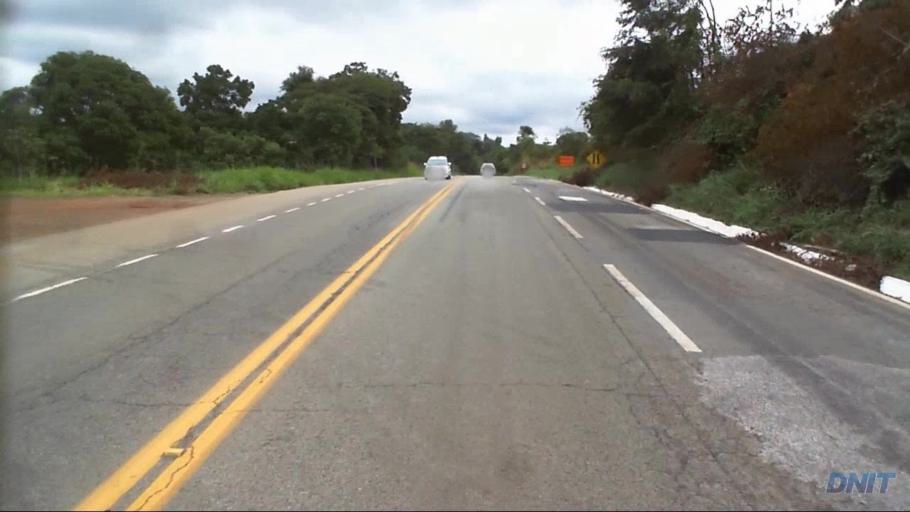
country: BR
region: Minas Gerais
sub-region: Barao De Cocais
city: Barao de Cocais
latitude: -19.7975
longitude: -43.4199
